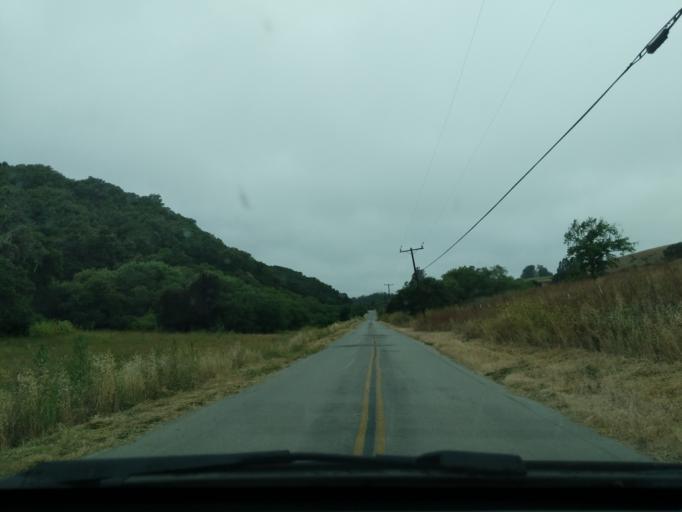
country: US
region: California
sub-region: San Benito County
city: San Juan Bautista
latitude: 36.8802
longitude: -121.5816
